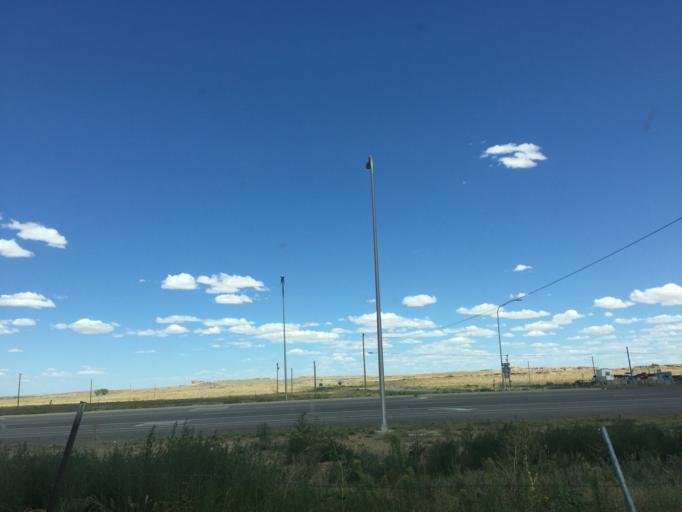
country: US
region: New Mexico
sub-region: San Juan County
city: Shiprock
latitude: 36.3349
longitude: -108.7128
